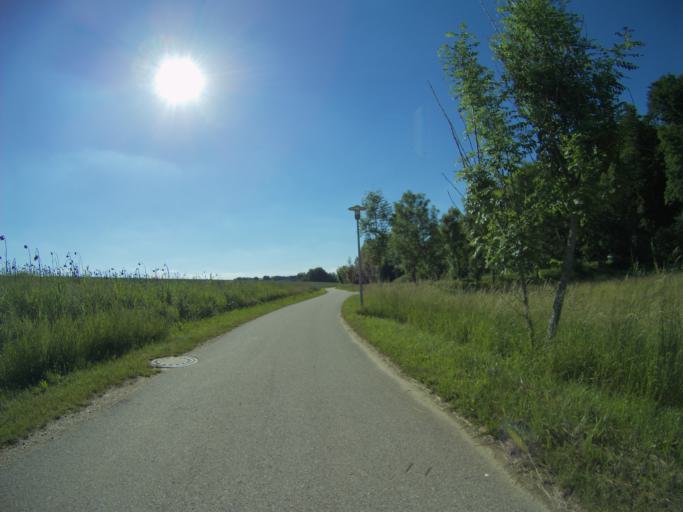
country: DE
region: Bavaria
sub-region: Upper Bavaria
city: Freising
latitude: 48.4036
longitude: 11.7066
